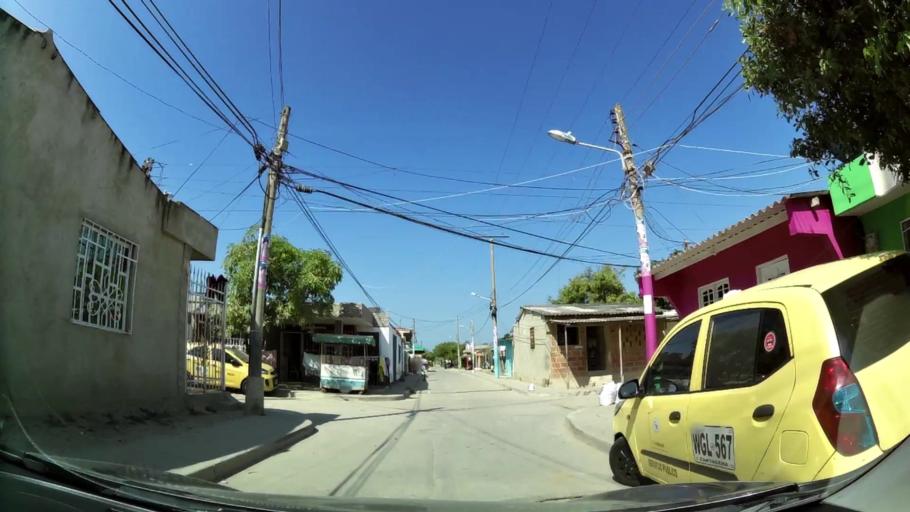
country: CO
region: Bolivar
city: Cartagena
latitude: 10.4114
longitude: -75.5138
